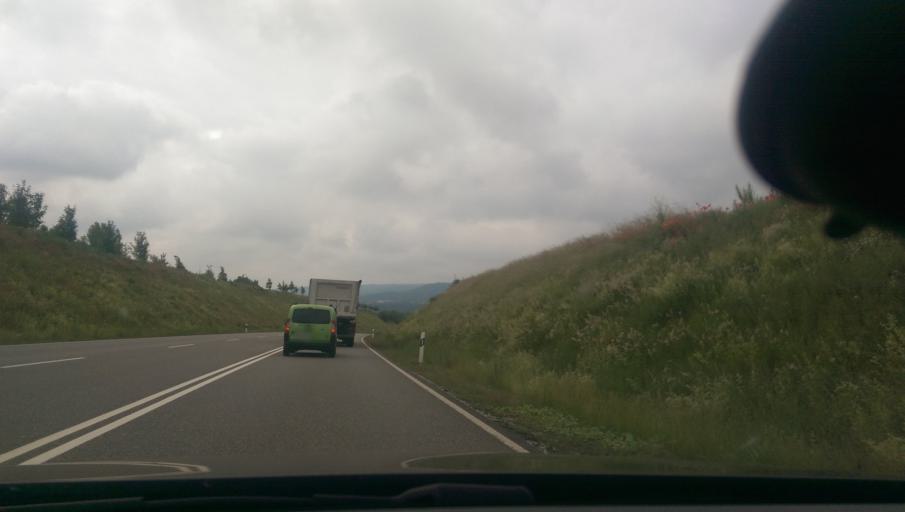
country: DE
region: Thuringia
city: Sondershausen
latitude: 51.3943
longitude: 10.8440
